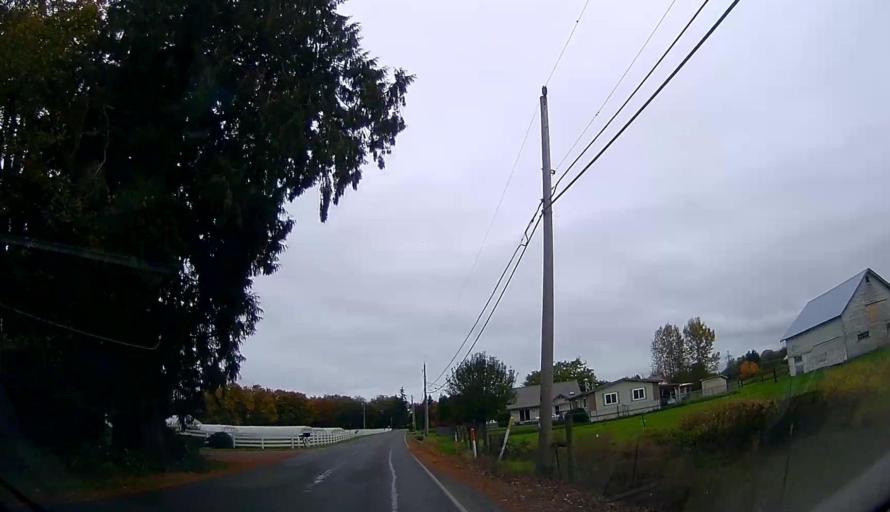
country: US
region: Washington
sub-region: Skagit County
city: Sedro-Woolley
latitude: 48.5047
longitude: -122.1937
